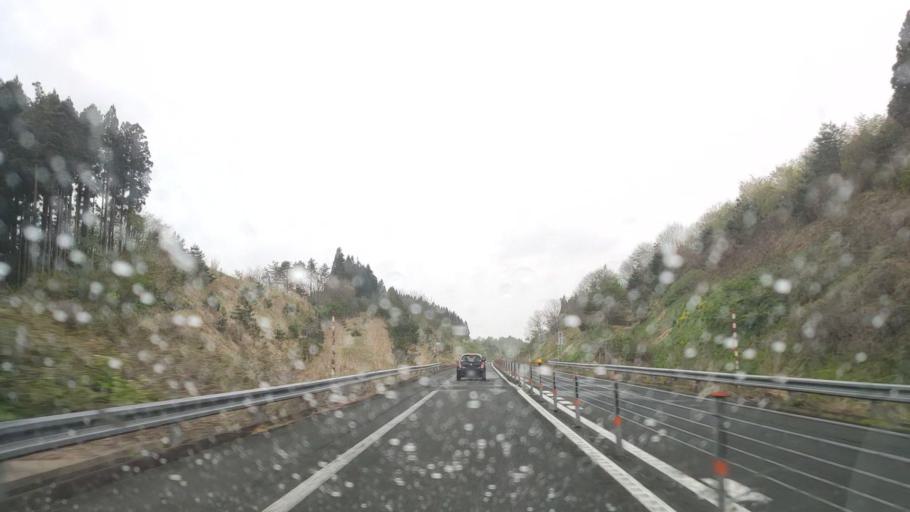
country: JP
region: Akita
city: Noshiromachi
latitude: 40.2048
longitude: 140.1614
